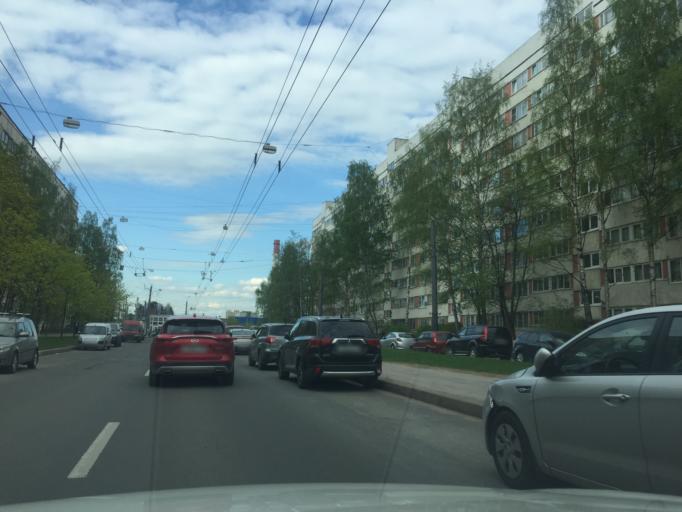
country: RU
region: Leningrad
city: Parnas
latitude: 60.0567
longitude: 30.3462
